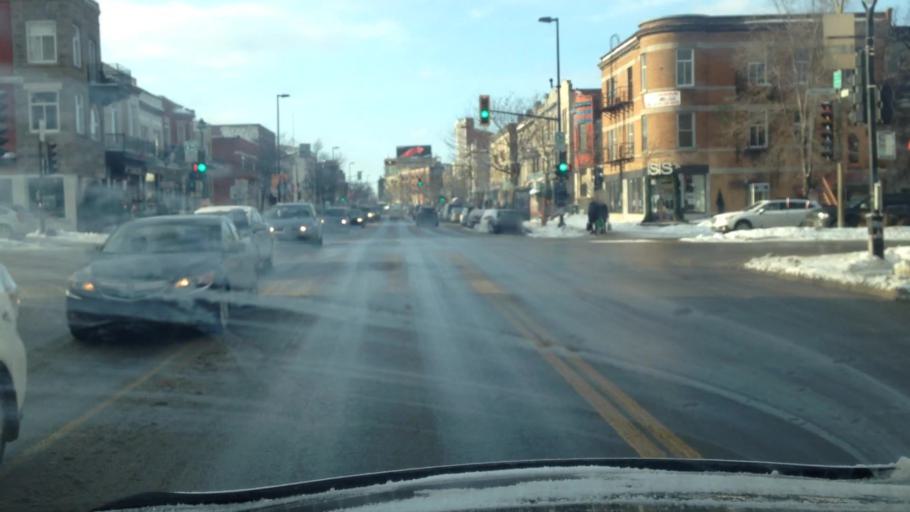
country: CA
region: Quebec
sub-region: Montreal
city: Montreal
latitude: 45.5189
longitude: -73.5941
